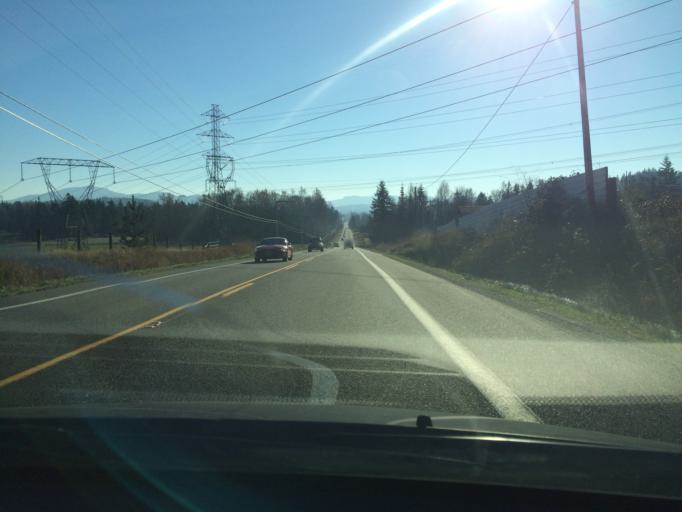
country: US
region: Washington
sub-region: Whatcom County
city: Bellingham
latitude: 48.8094
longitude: -122.4431
